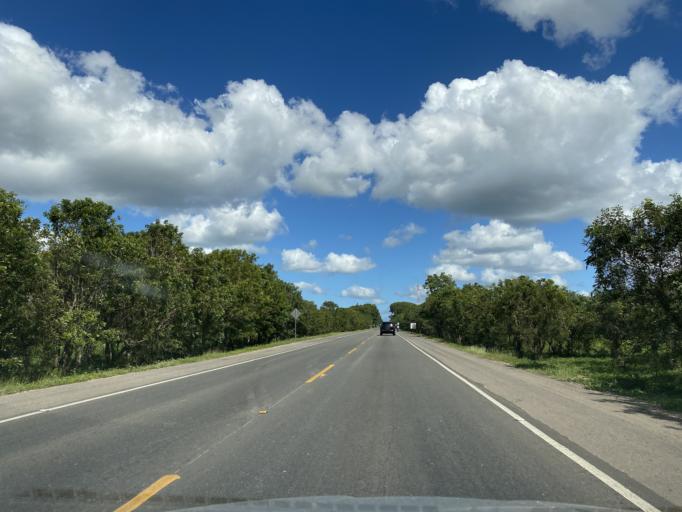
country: DO
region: Monte Plata
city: Monte Plata
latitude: 18.7638
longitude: -69.7602
